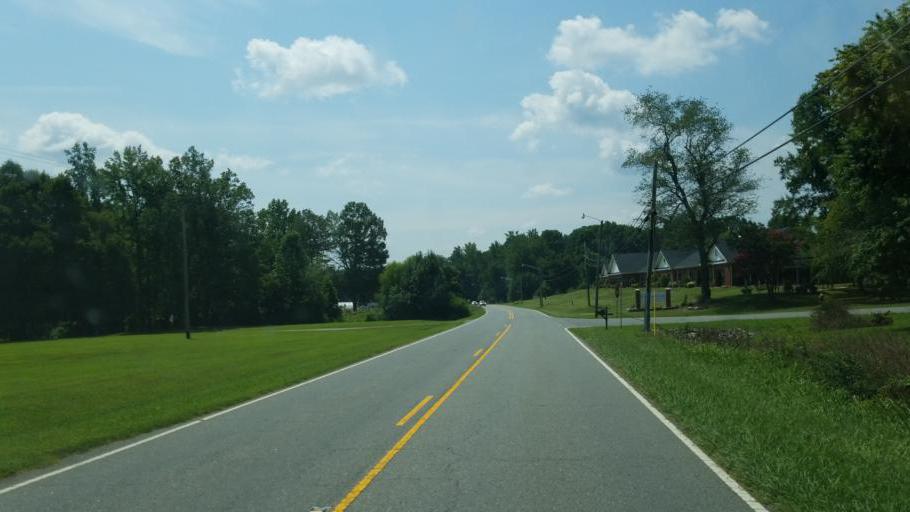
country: US
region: North Carolina
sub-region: Gaston County
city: Cherryville
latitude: 35.3949
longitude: -81.3933
